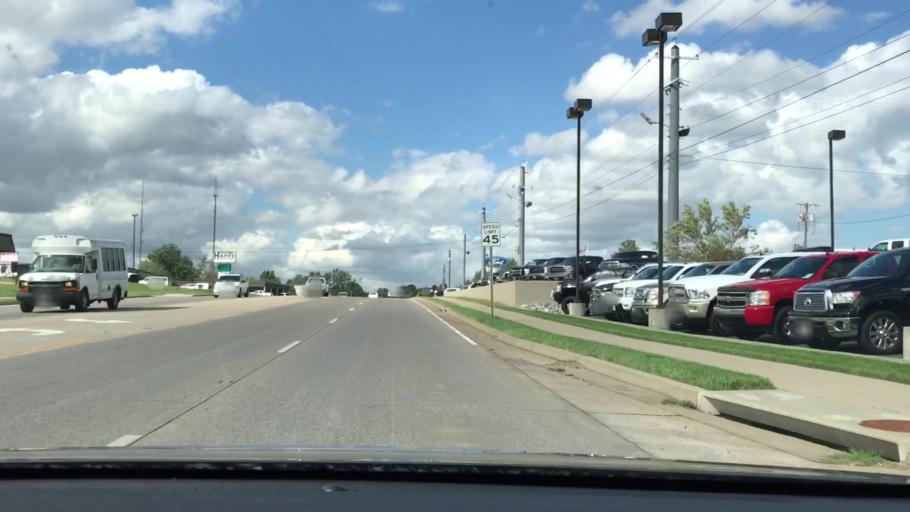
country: US
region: Kentucky
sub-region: Graves County
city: Mayfield
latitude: 36.7594
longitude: -88.6415
